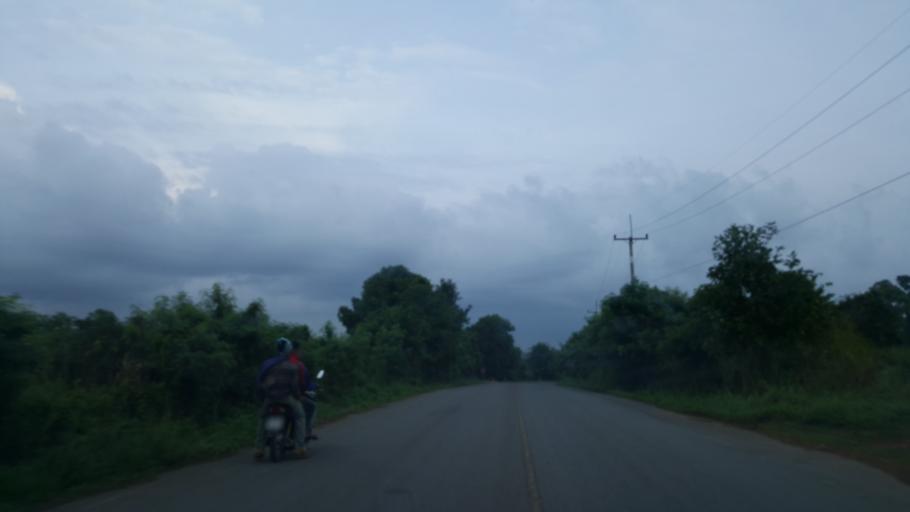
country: TH
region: Chon Buri
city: Sattahip
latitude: 12.7215
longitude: 100.9170
